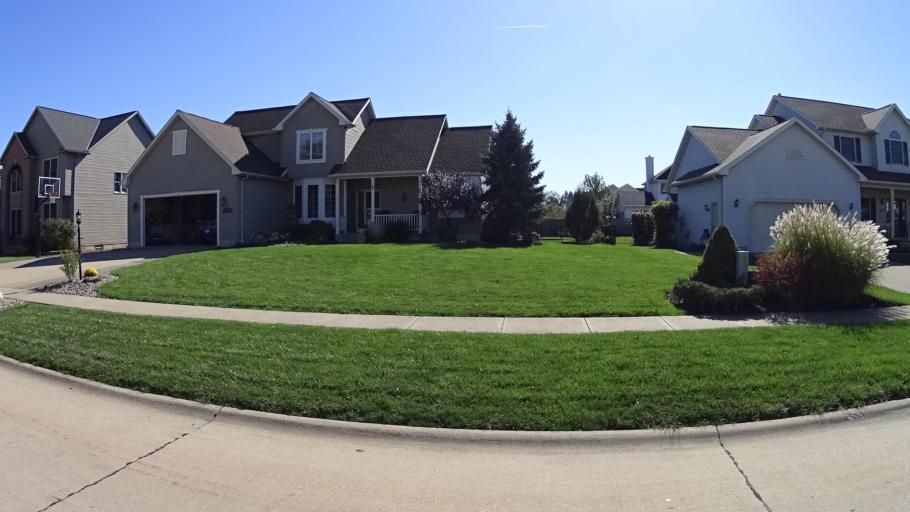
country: US
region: Ohio
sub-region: Lorain County
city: Amherst
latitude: 41.3879
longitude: -82.2215
